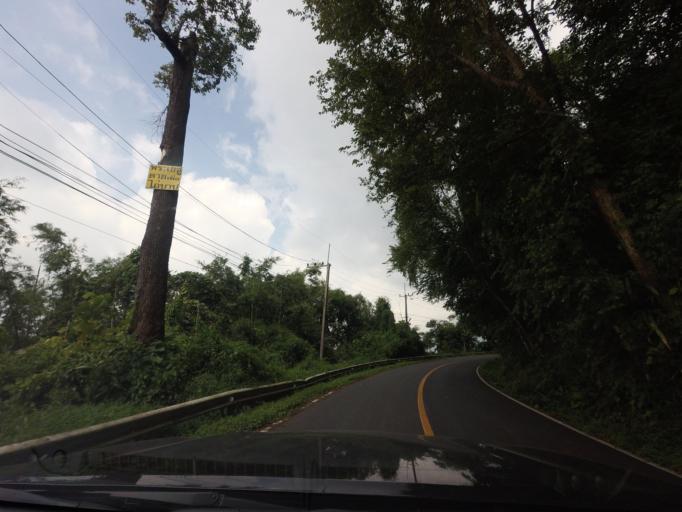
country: TH
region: Nan
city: Pua
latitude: 19.1898
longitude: 101.0288
